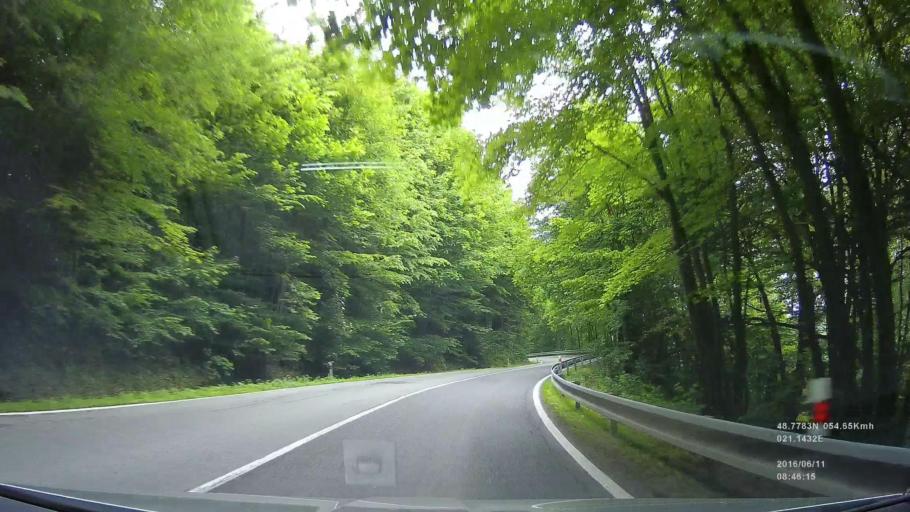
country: SK
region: Kosicky
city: Kosice
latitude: 48.7746
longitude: 21.1483
